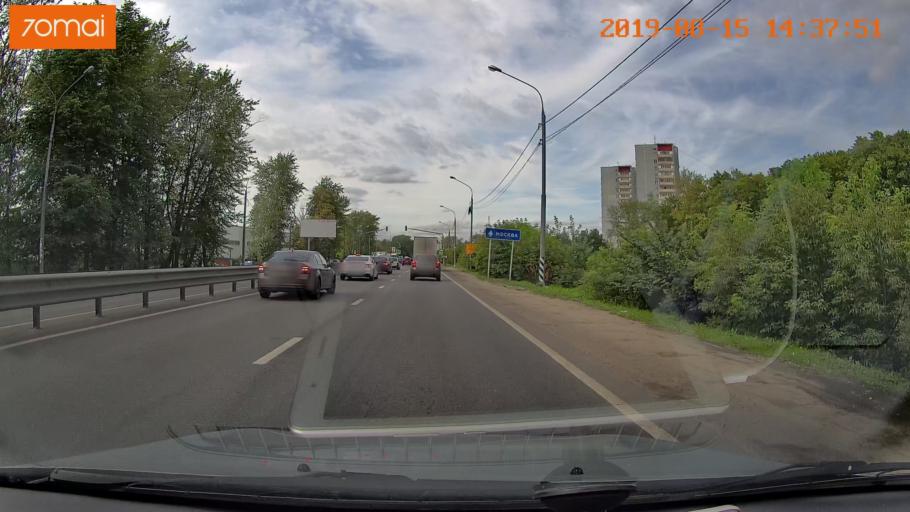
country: RU
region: Moskovskaya
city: Tomilino
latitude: 55.6550
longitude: 37.9229
